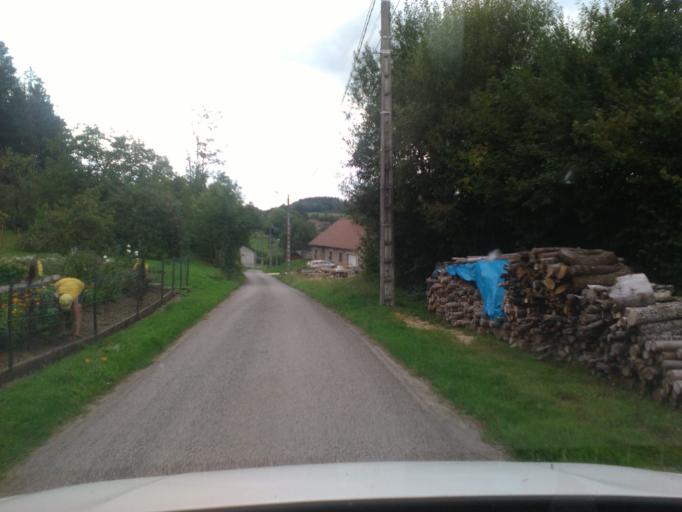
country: FR
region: Lorraine
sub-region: Departement des Vosges
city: Senones
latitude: 48.3348
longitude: 7.0221
